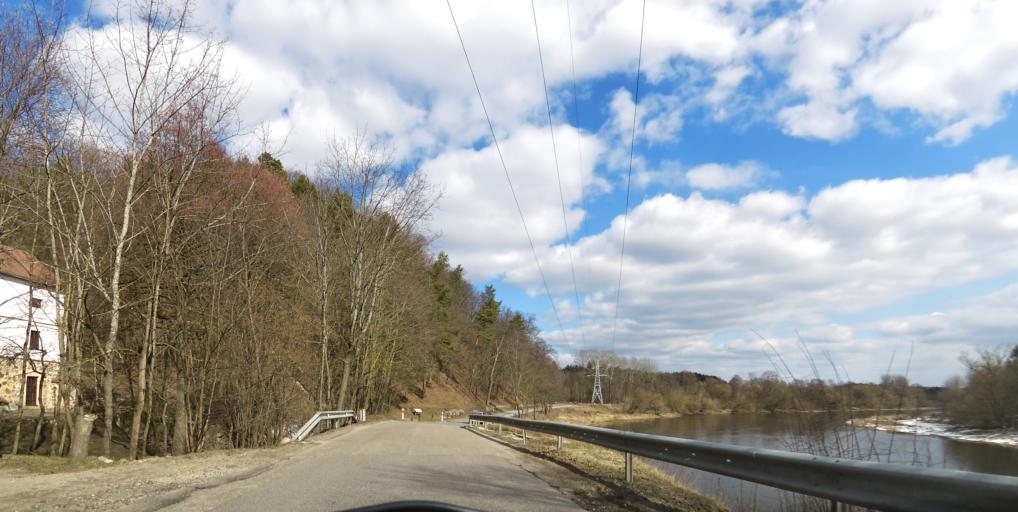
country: LT
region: Vilnius County
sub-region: Vilnius
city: Fabijoniskes
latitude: 54.7452
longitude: 25.2911
